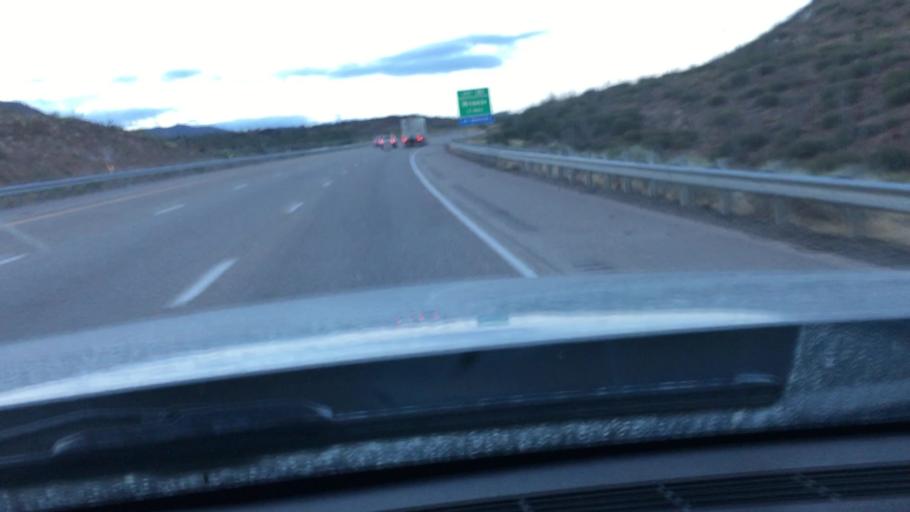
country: US
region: Utah
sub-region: Washington County
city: Toquerville
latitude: 37.3057
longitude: -113.2976
